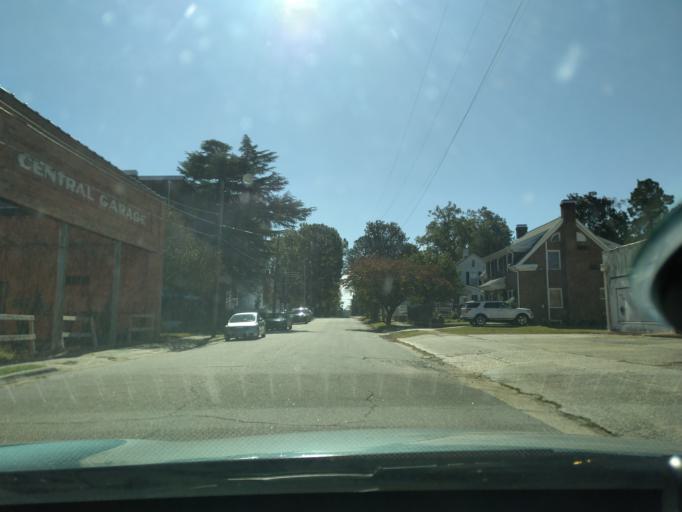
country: US
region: North Carolina
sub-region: Washington County
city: Plymouth
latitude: 35.8674
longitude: -76.7494
